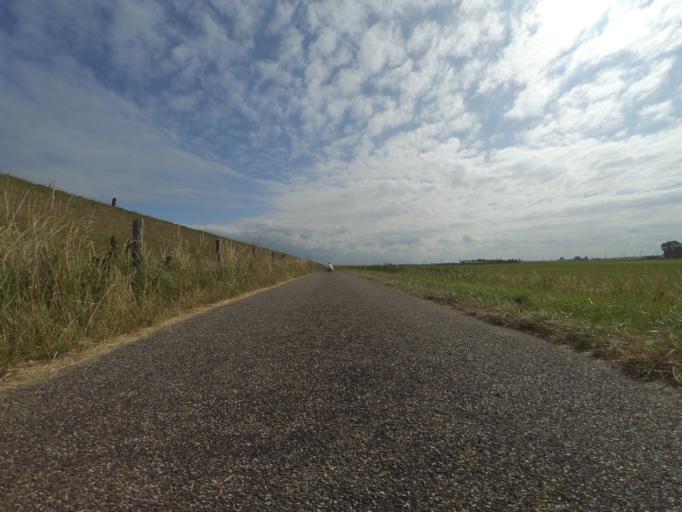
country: NL
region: Zeeland
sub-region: Gemeente Reimerswaal
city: Yerseke
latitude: 51.4306
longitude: 4.1499
